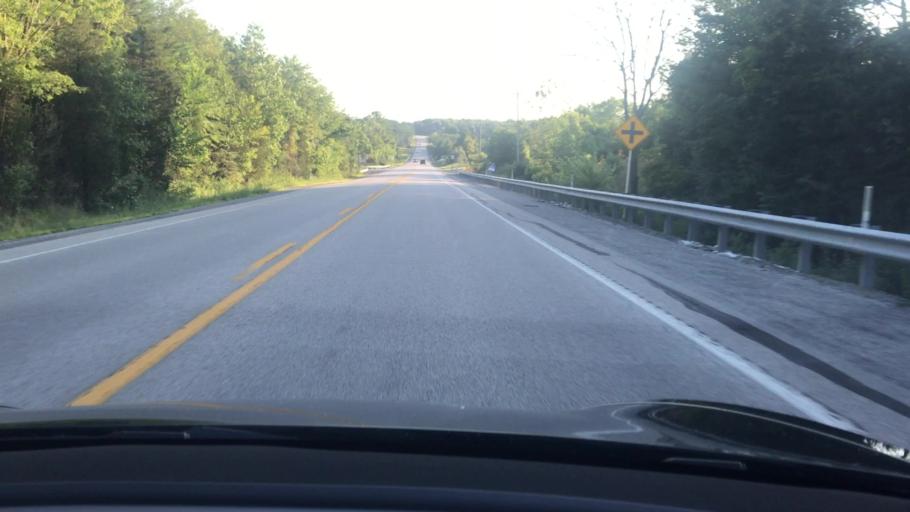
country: US
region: Pennsylvania
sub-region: York County
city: Valley Green
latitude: 40.1002
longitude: -76.8717
